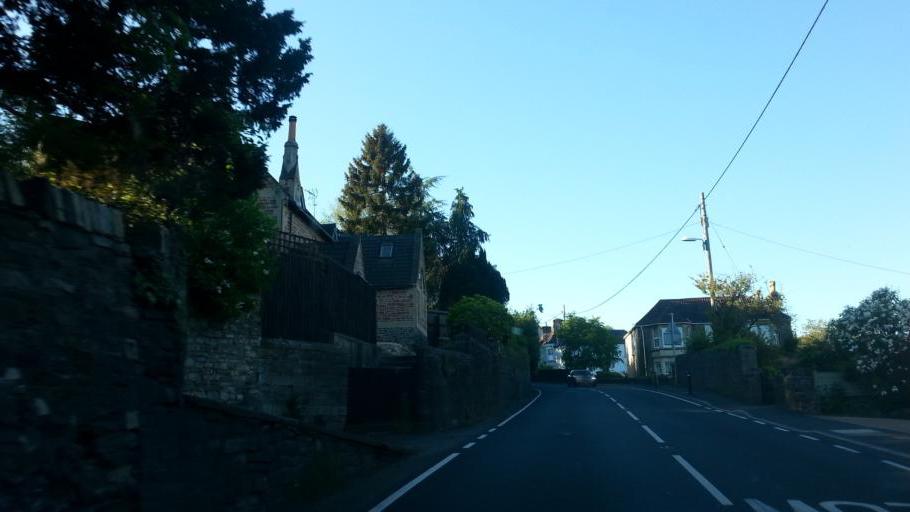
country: GB
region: England
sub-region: Bath and North East Somerset
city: Publow
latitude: 51.3729
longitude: -2.5505
